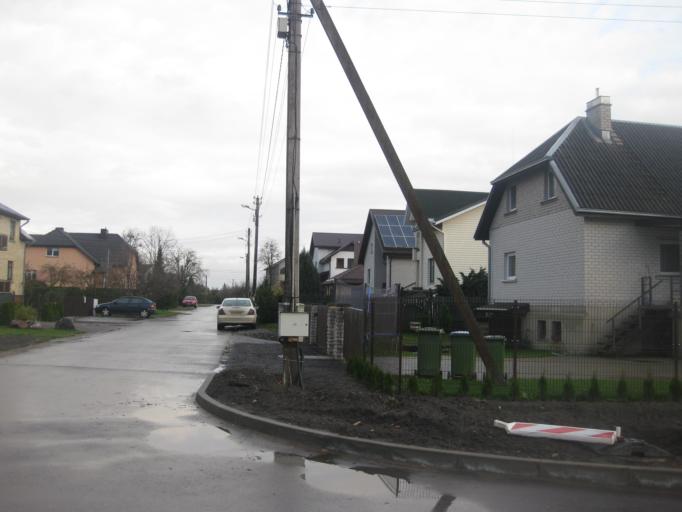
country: LT
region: Kauno apskritis
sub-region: Kaunas
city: Aleksotas
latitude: 54.8566
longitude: 23.8894
